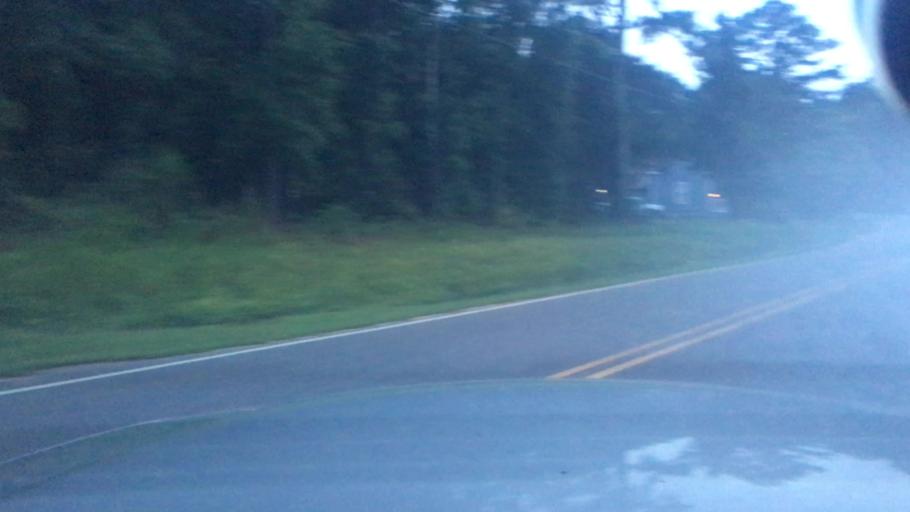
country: US
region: North Carolina
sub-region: Cumberland County
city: Hope Mills
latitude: 34.9604
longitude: -78.9239
